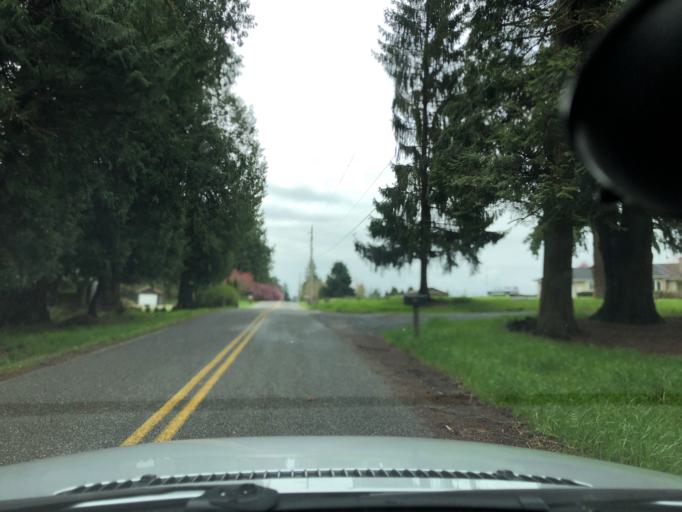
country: US
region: Washington
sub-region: Whatcom County
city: Lynden
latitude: 48.9871
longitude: -122.5185
